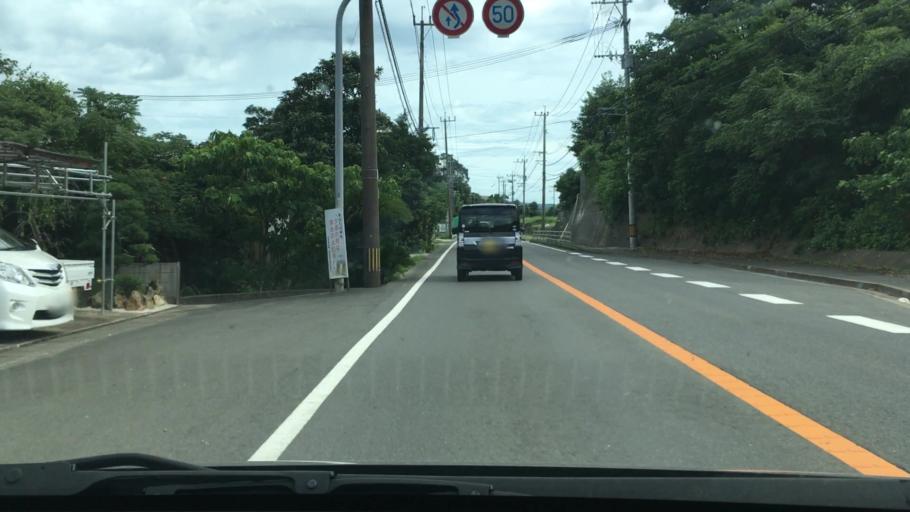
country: JP
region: Nagasaki
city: Togitsu
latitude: 32.8855
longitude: 129.7900
